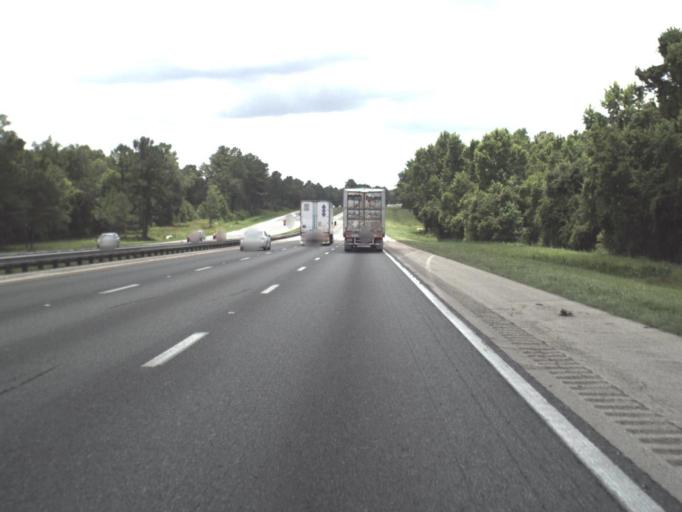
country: US
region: Florida
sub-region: Alachua County
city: Gainesville
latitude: 29.5191
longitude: -82.3074
